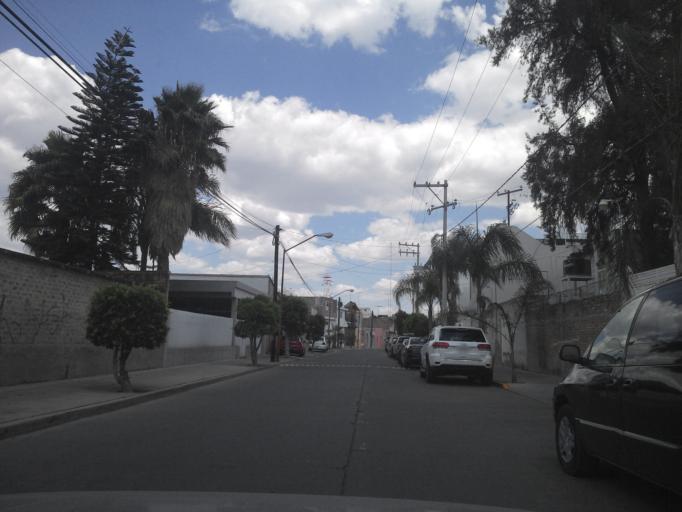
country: MX
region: Guanajuato
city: San Francisco del Rincon
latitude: 21.0207
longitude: -101.8632
